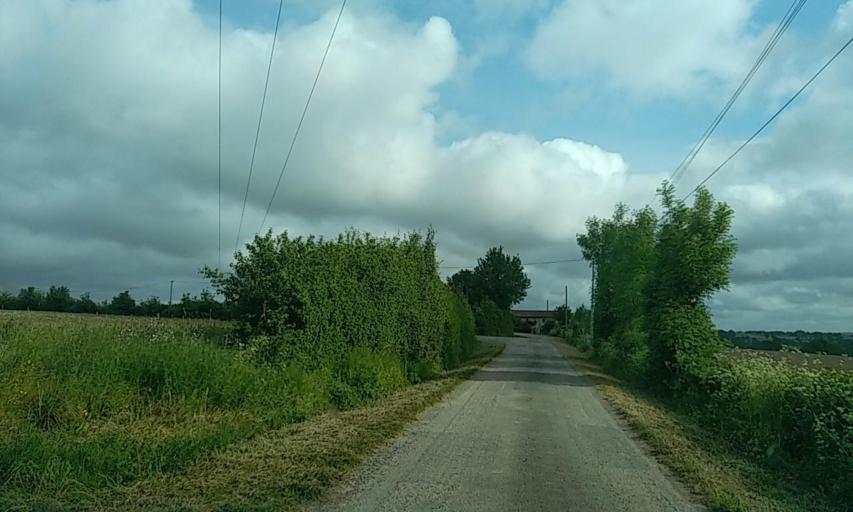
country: FR
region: Poitou-Charentes
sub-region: Departement des Deux-Sevres
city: Boisme
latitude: 46.7633
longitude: -0.4167
